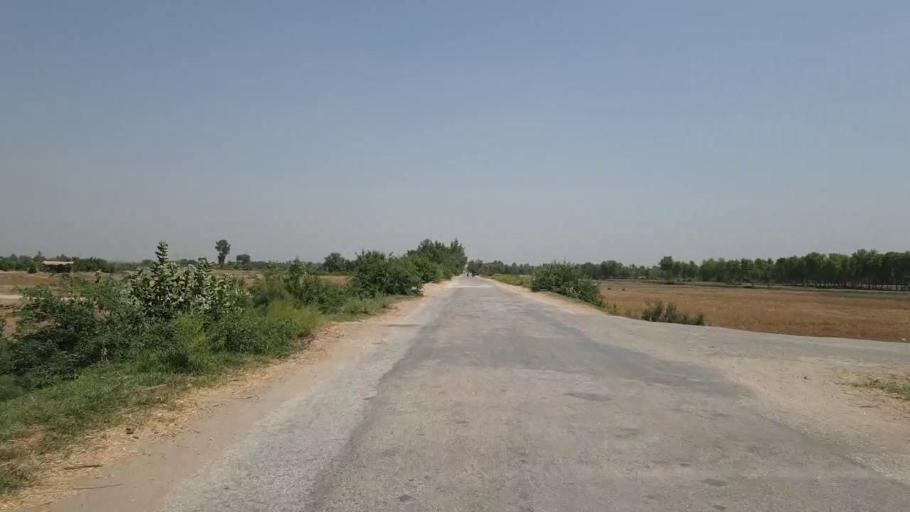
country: PK
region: Sindh
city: Adilpur
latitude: 27.9070
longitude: 69.2974
